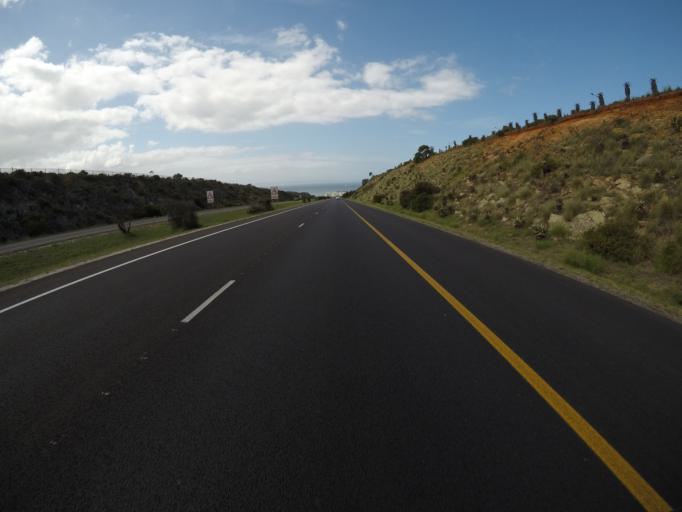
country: ZA
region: Western Cape
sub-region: Eden District Municipality
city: Mossel Bay
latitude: -34.1626
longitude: 22.0930
